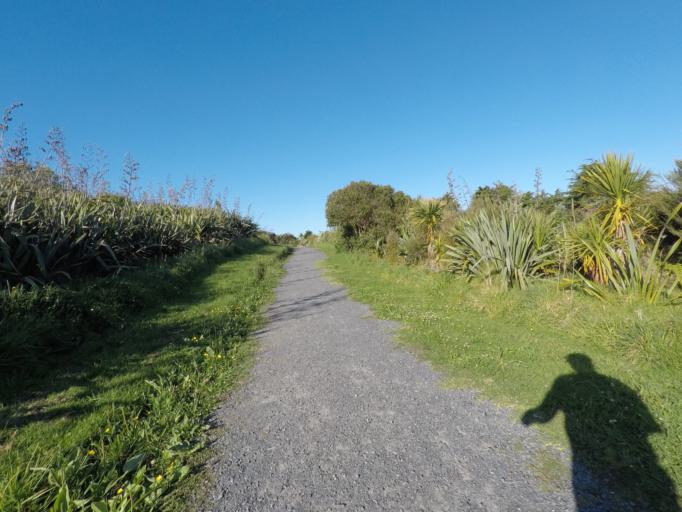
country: NZ
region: Auckland
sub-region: Auckland
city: Rosebank
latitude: -36.8415
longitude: 174.6589
